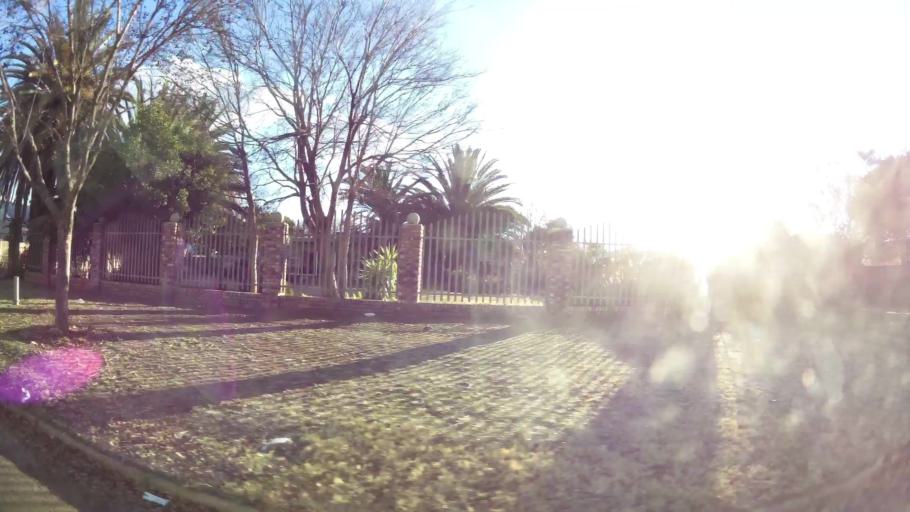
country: ZA
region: North-West
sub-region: Dr Kenneth Kaunda District Municipality
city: Potchefstroom
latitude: -26.7307
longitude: 27.0895
